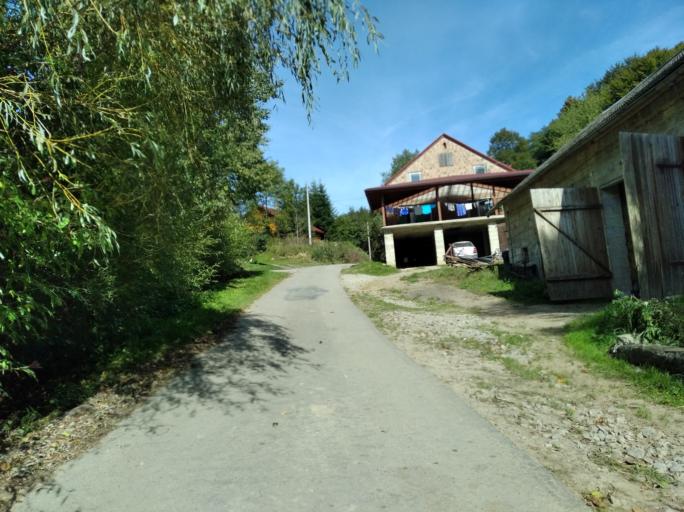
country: PL
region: Subcarpathian Voivodeship
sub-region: Powiat ropczycko-sedziszowski
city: Wielopole Skrzynskie
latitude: 49.9098
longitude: 21.6237
